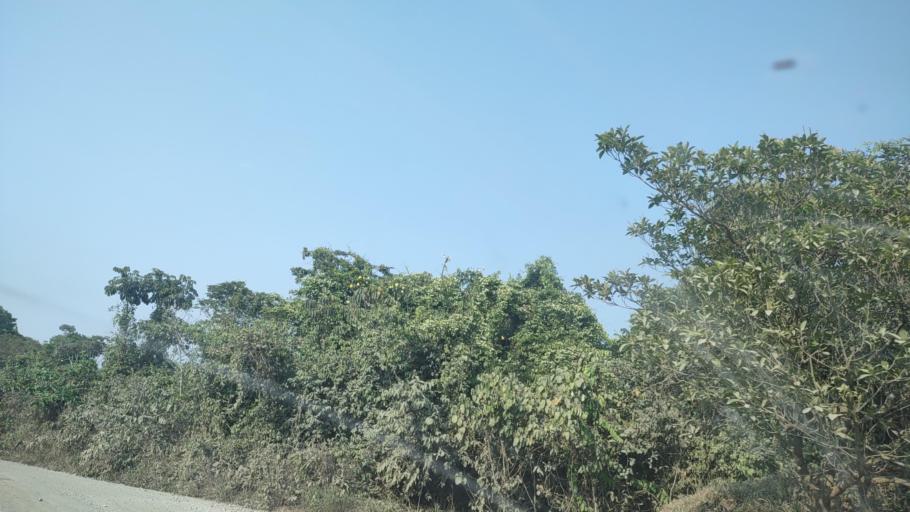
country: MX
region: Tabasco
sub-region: Huimanguillo
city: Francisco Rueda
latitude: 17.6442
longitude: -93.9084
